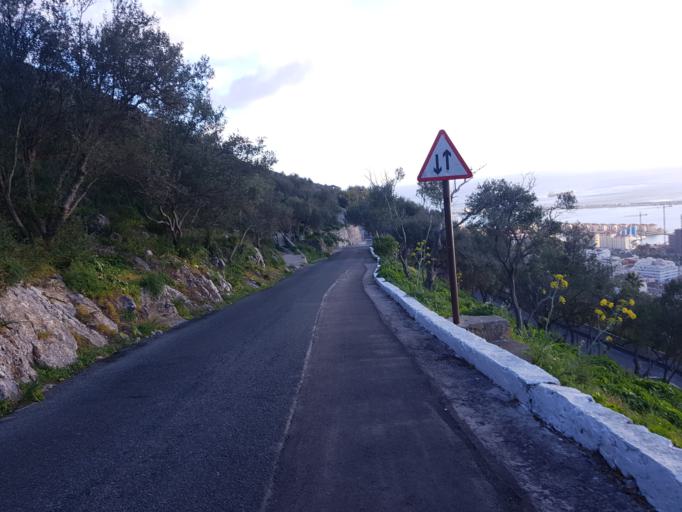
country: GI
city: Gibraltar
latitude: 36.1438
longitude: -5.3484
